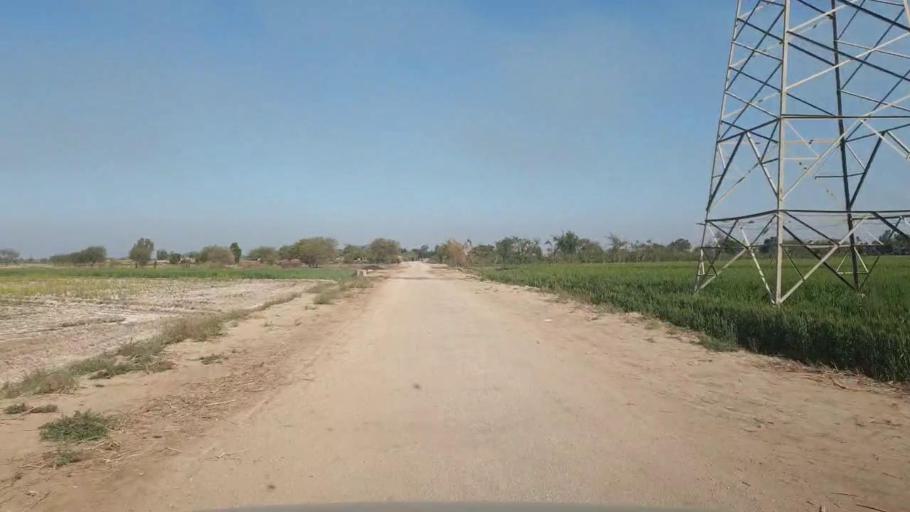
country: PK
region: Sindh
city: Mirwah Gorchani
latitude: 25.3058
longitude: 69.0929
